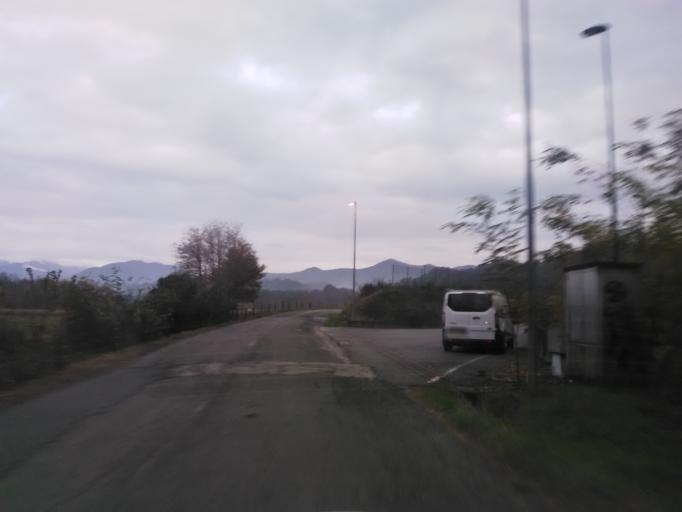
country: IT
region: Piedmont
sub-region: Provincia di Novara
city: Prato Sesia
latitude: 45.6596
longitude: 8.3763
